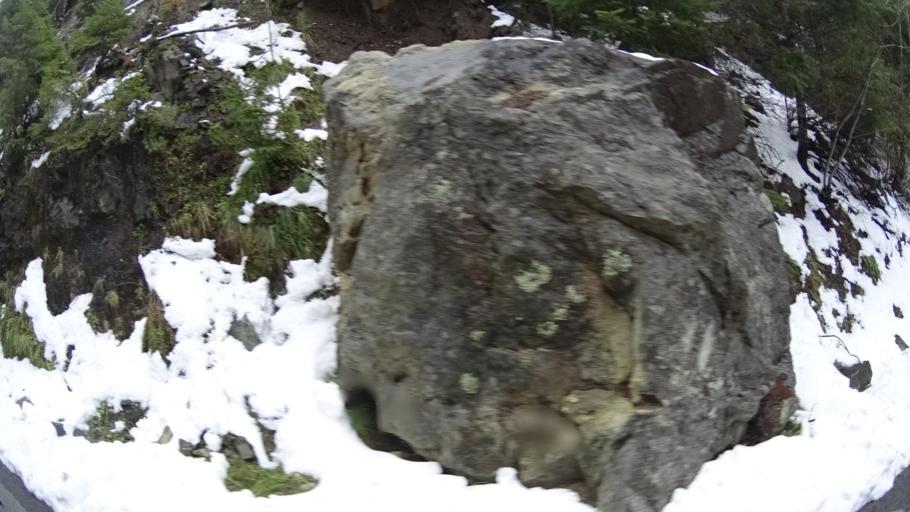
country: US
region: California
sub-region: Humboldt County
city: Willow Creek
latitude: 40.8732
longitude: -123.7555
